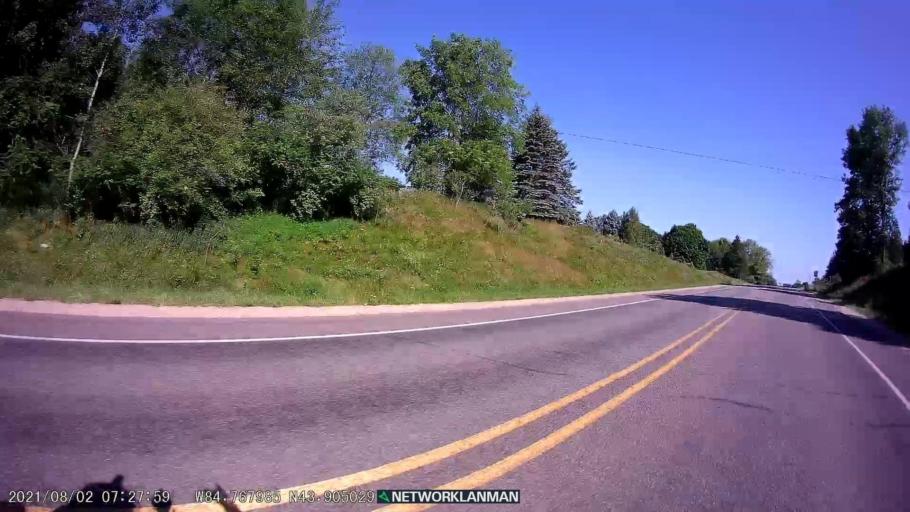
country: US
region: Michigan
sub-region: Clare County
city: Clare
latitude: 43.9050
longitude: -84.7680
